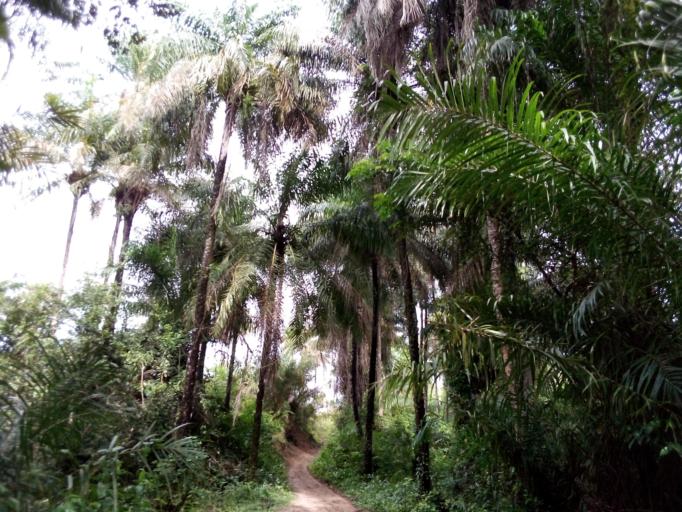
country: SL
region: Southern Province
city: Bonthe
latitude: 7.5106
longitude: -12.5522
